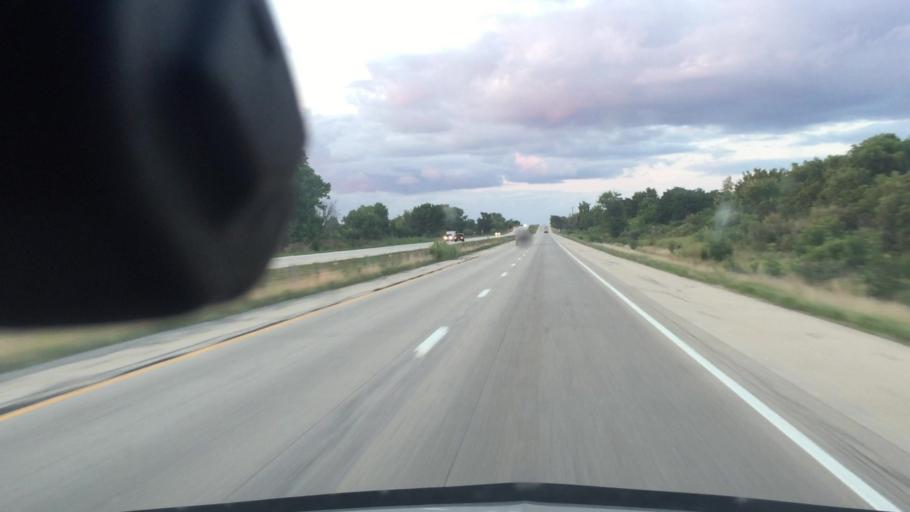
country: US
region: Illinois
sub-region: Grundy County
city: Central City
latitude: 41.2165
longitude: -88.2889
